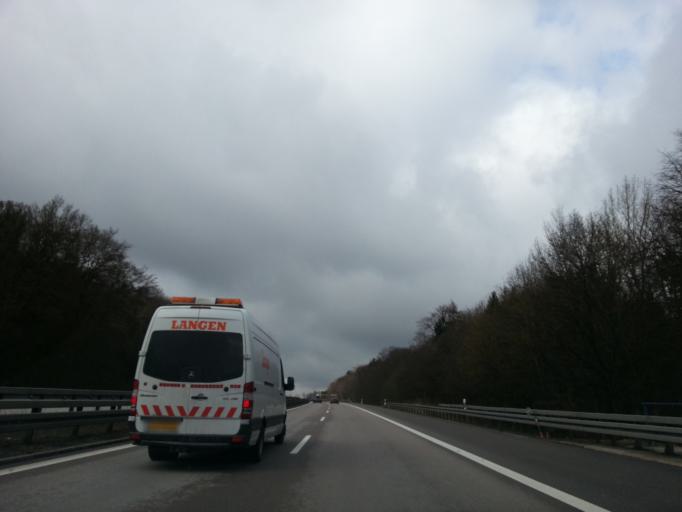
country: DE
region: Bavaria
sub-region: Upper Palatinate
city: Brunn
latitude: 49.1246
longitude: 11.8710
